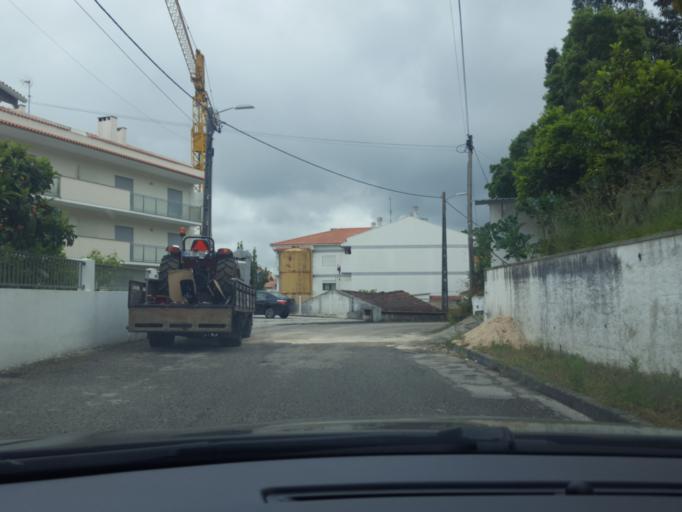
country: PT
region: Leiria
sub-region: Leiria
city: Leiria
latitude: 39.7329
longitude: -8.7919
